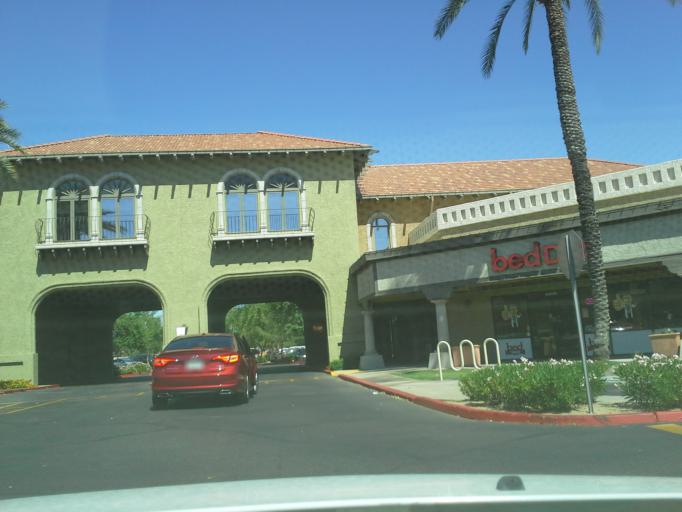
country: US
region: Arizona
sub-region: Maricopa County
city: Paradise Valley
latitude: 33.5852
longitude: -111.9246
